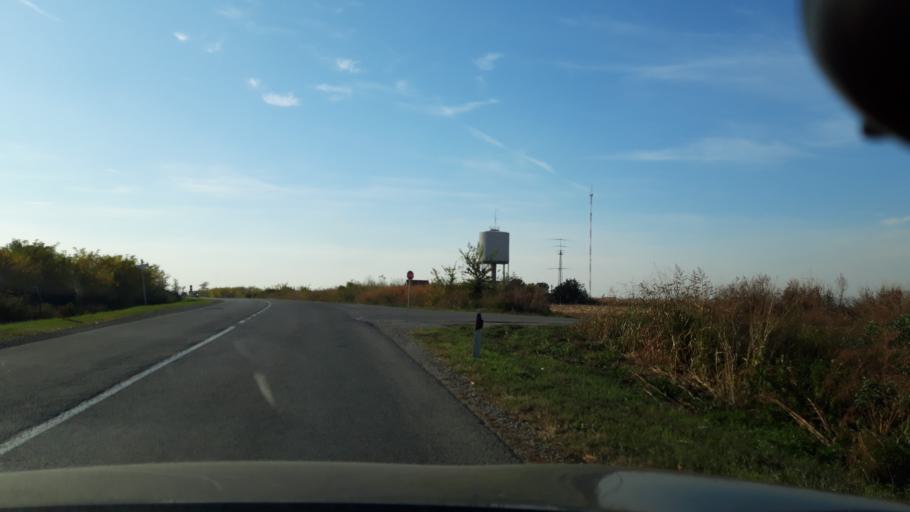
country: RS
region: Autonomna Pokrajina Vojvodina
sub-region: Sremski Okrug
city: Ruma
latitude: 45.0105
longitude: 19.8823
